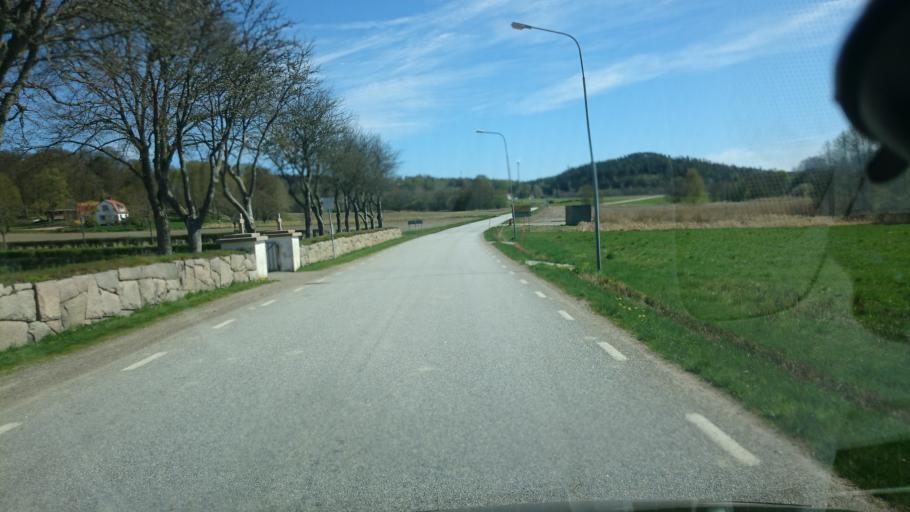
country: SE
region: Vaestra Goetaland
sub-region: Munkedals Kommun
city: Munkedal
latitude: 58.3794
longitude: 11.6714
